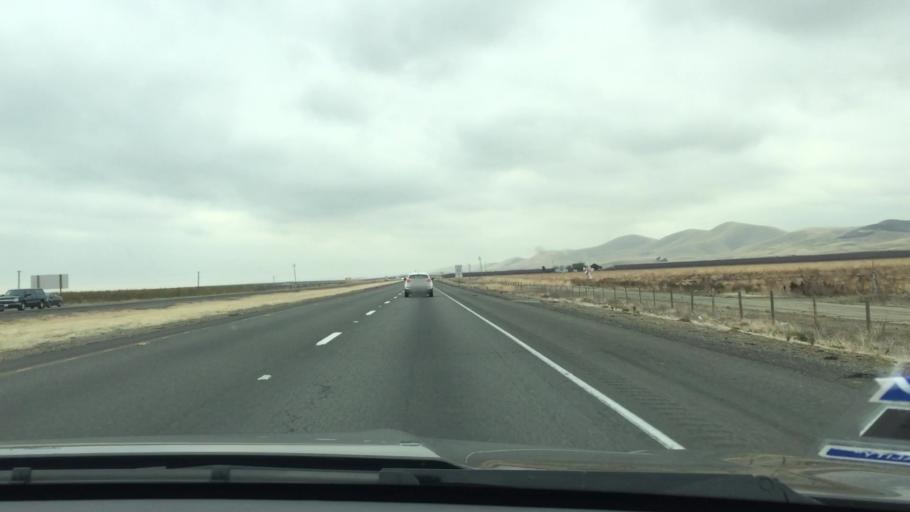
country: US
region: California
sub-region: Merced County
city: Gustine
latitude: 37.2397
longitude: -121.0875
